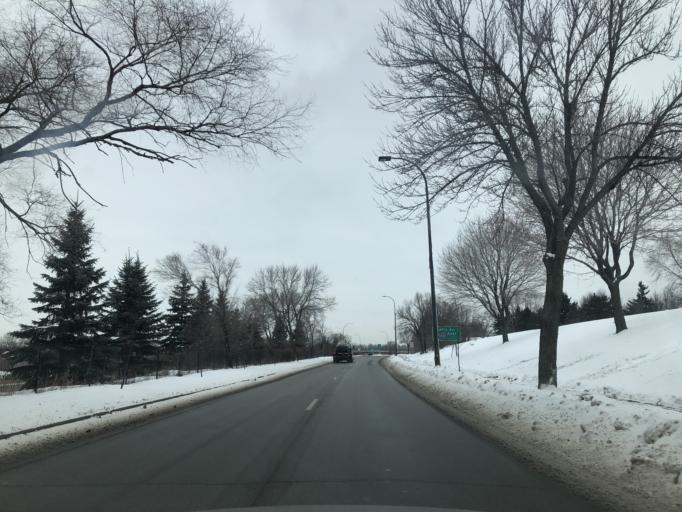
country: US
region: Minnesota
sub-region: Anoka County
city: Columbia Heights
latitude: 45.0488
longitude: -93.2852
